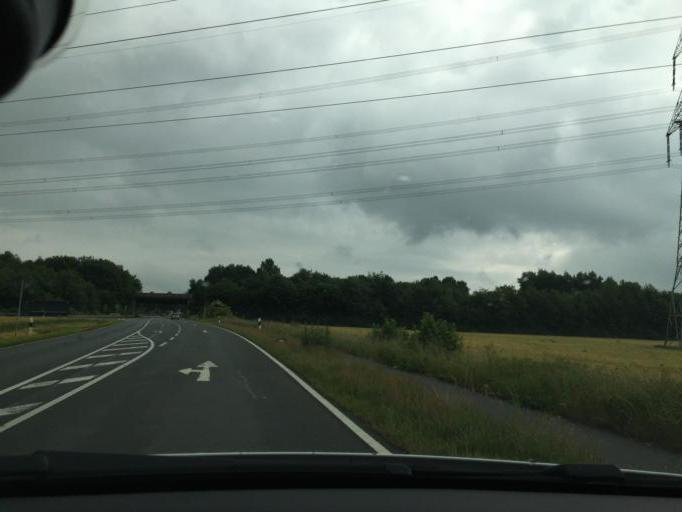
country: DE
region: Lower Saxony
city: Hameln
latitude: 52.0437
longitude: 9.3685
